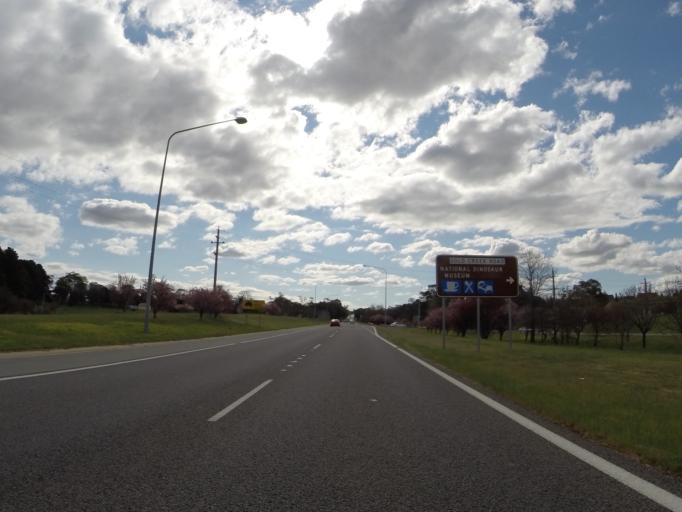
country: AU
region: Australian Capital Territory
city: Belconnen
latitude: -35.1954
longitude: 149.0870
